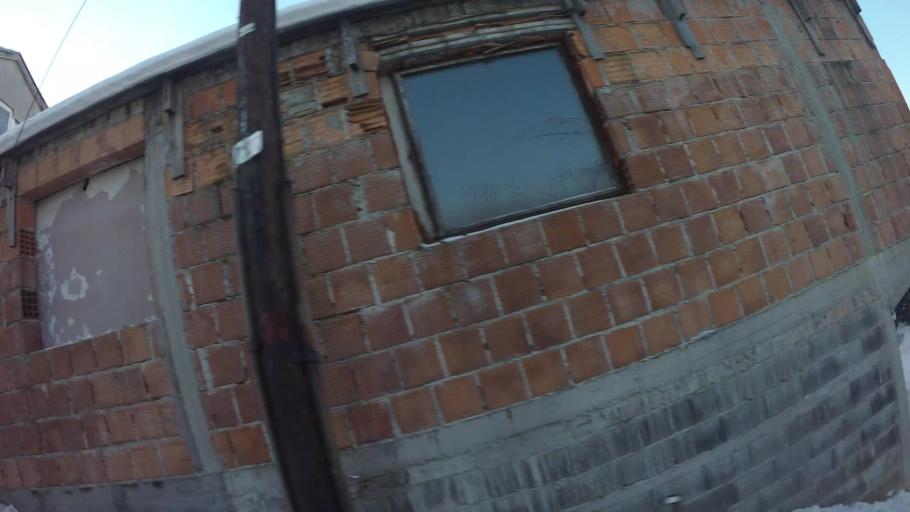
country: BA
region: Federation of Bosnia and Herzegovina
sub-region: Kanton Sarajevo
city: Sarajevo
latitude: 43.8408
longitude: 18.3630
